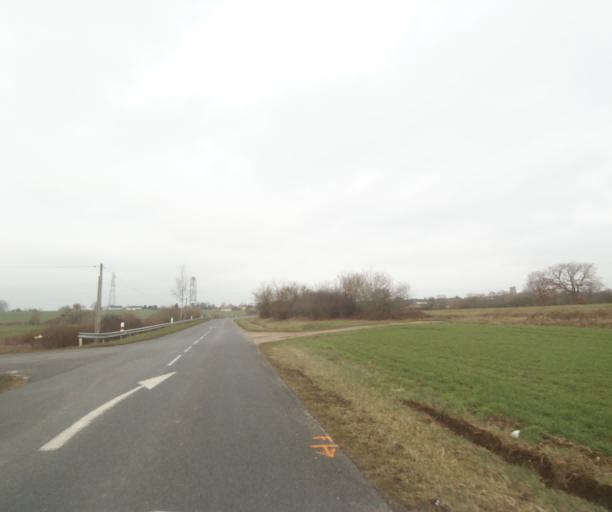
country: FR
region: Champagne-Ardenne
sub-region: Departement de la Marne
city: Pargny-sur-Saulx
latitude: 48.7422
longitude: 4.8504
